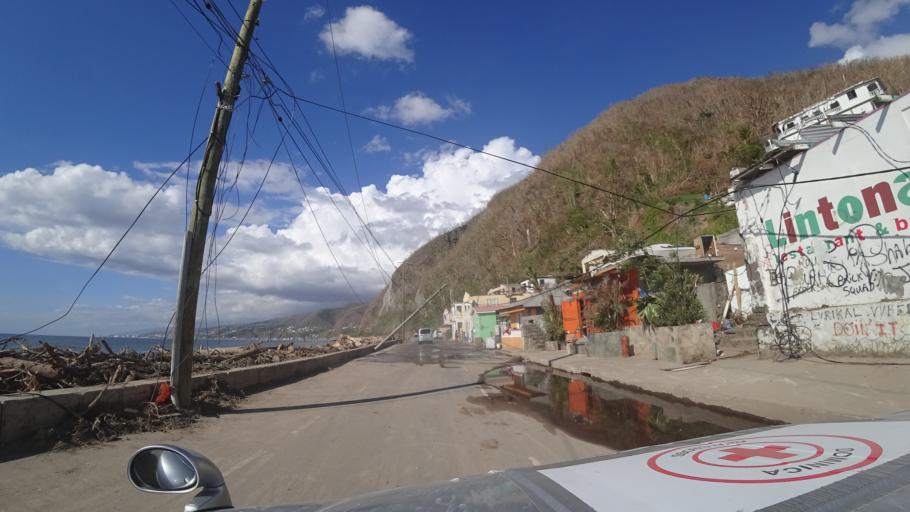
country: DM
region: Saint Luke
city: Pointe Michel
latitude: 15.2650
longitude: -61.3767
